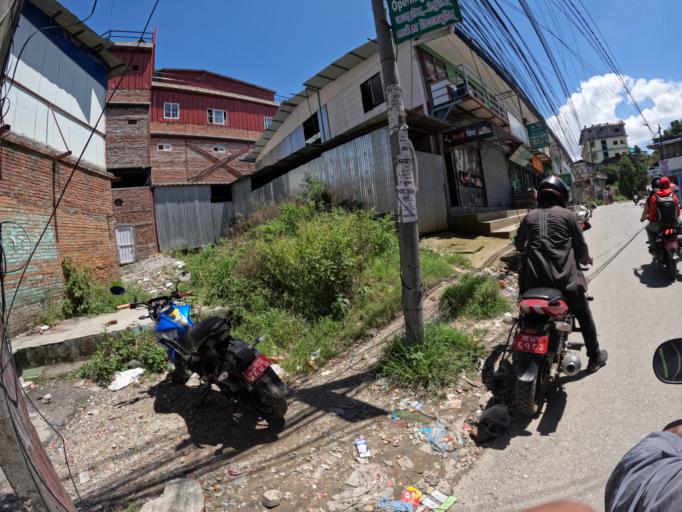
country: NP
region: Central Region
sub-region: Bagmati Zone
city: Kathmandu
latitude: 27.7463
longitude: 85.3270
